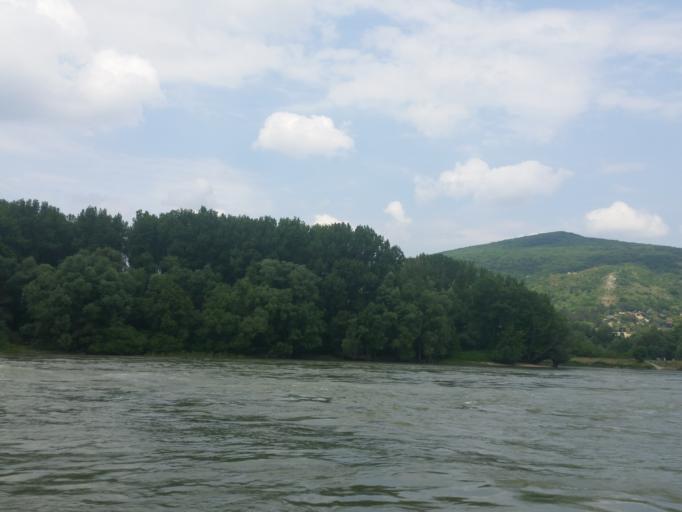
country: AT
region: Lower Austria
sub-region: Politischer Bezirk Bruck an der Leitha
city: Hainburg an der Donau
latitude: 48.1728
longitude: 16.9732
